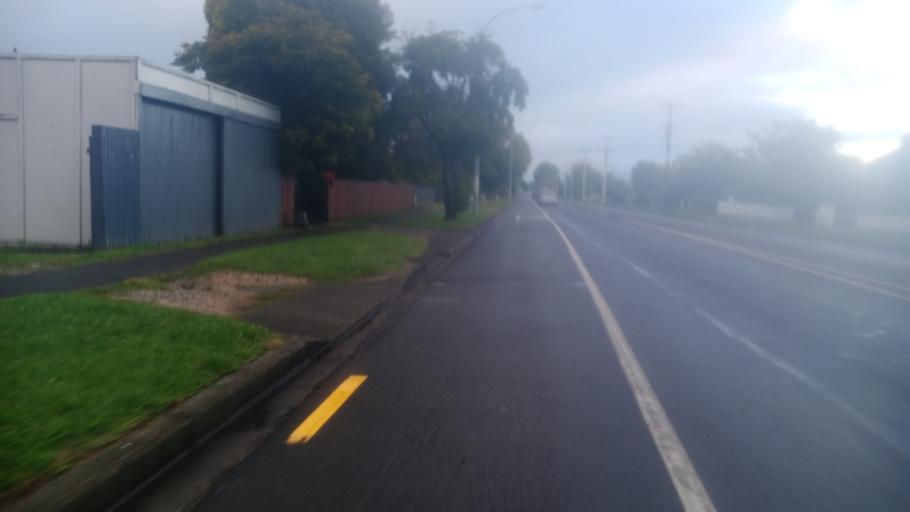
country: NZ
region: Gisborne
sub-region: Gisborne District
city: Gisborne
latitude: -38.6521
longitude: 177.9979
